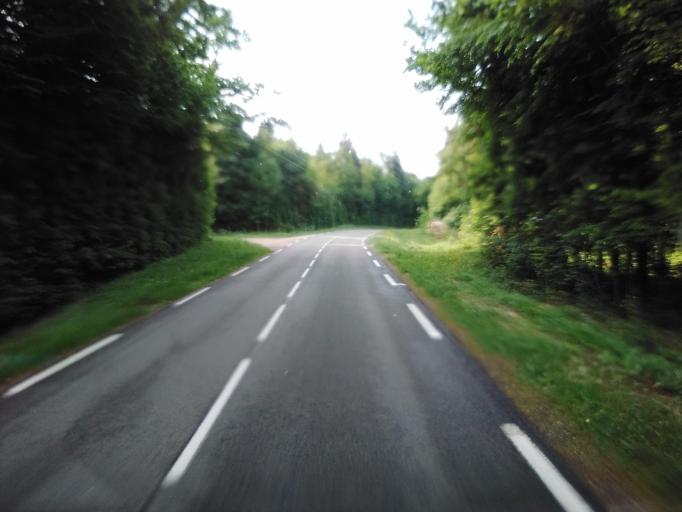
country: FR
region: Franche-Comte
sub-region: Departement du Jura
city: Arbois
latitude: 46.8439
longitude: 5.8178
